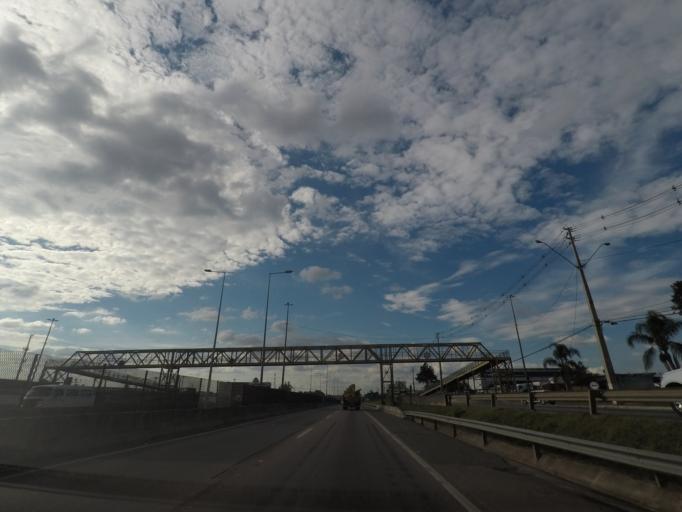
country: BR
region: Parana
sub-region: Sao Jose Dos Pinhais
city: Sao Jose dos Pinhais
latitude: -25.5518
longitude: -49.3051
